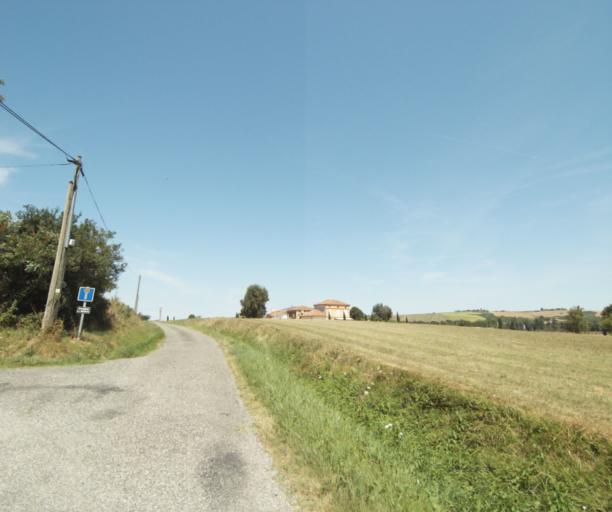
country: FR
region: Midi-Pyrenees
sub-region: Departement de l'Ariege
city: Lezat-sur-Leze
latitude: 43.2832
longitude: 1.3439
